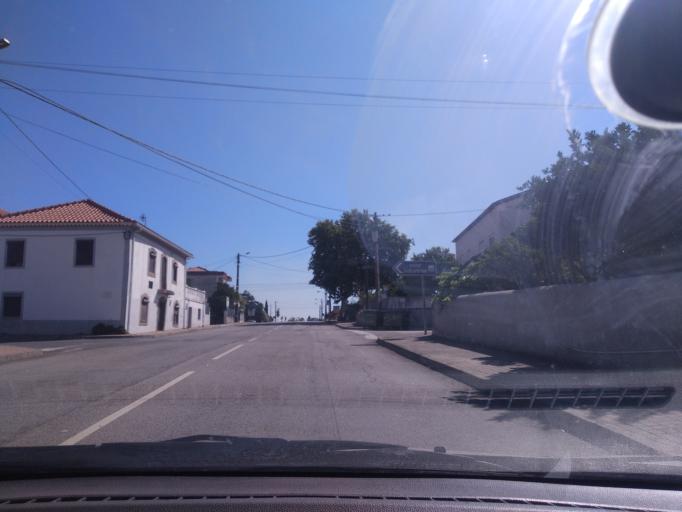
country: PT
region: Portalegre
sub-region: Nisa
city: Nisa
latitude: 39.6554
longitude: -7.6671
